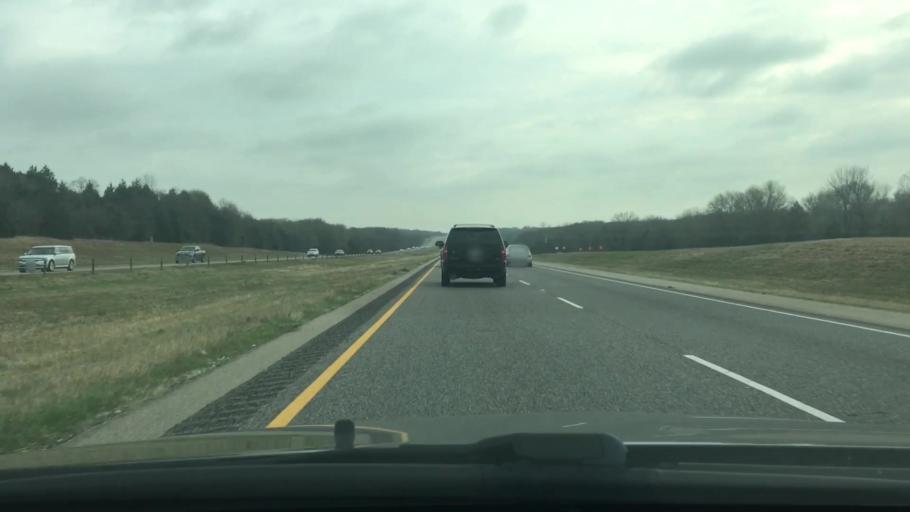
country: US
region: Texas
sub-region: Freestone County
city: Fairfield
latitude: 31.6591
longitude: -96.1616
